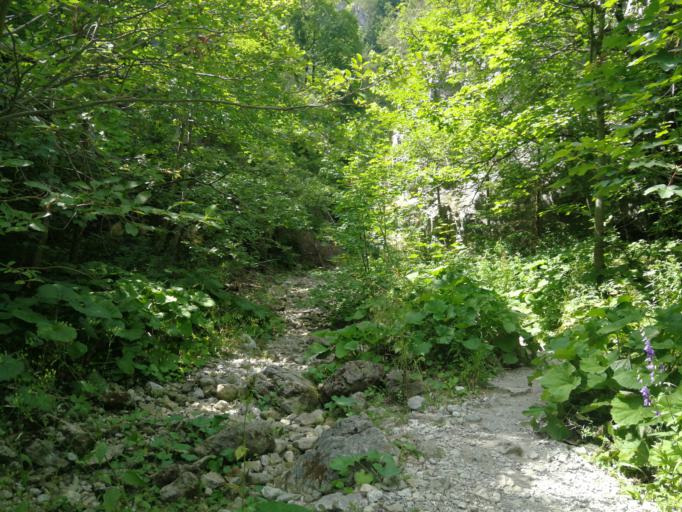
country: SK
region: Zilinsky
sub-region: Okres Liptovsky Mikulas
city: Liptovsky Mikulas
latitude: 49.1615
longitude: 19.4914
